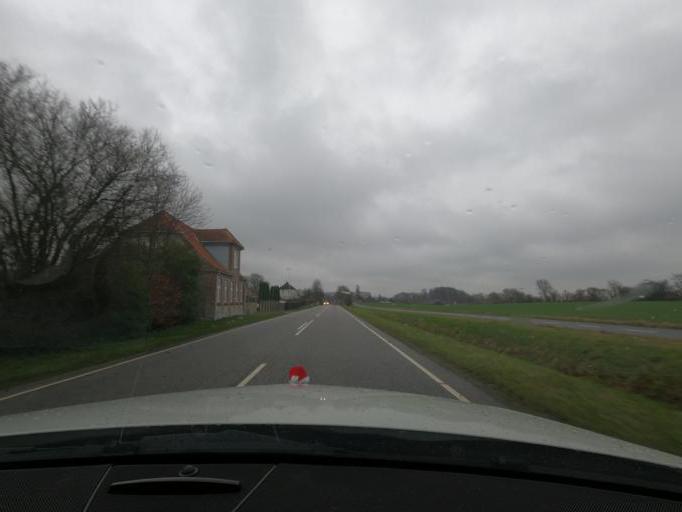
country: DK
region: South Denmark
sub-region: Haderslev Kommune
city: Starup
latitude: 55.2538
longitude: 9.6310
